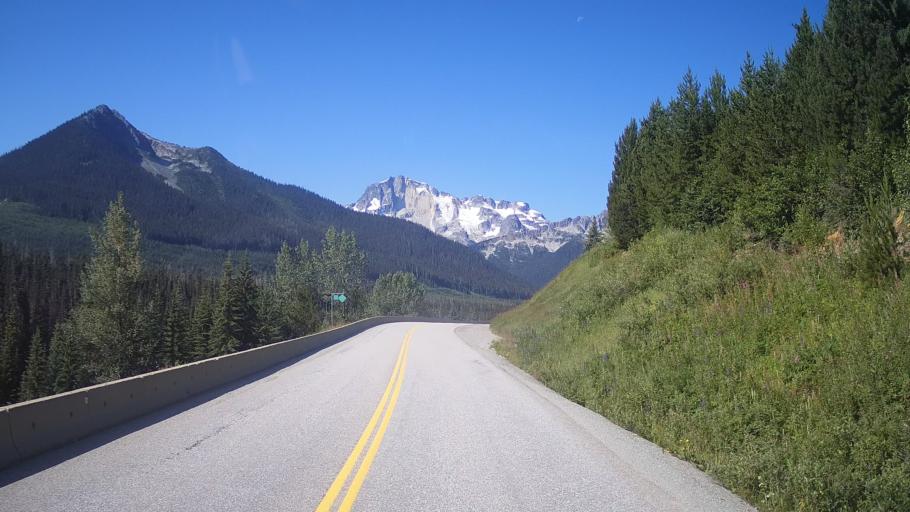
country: CA
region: British Columbia
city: Pemberton
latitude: 50.3856
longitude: -122.3754
